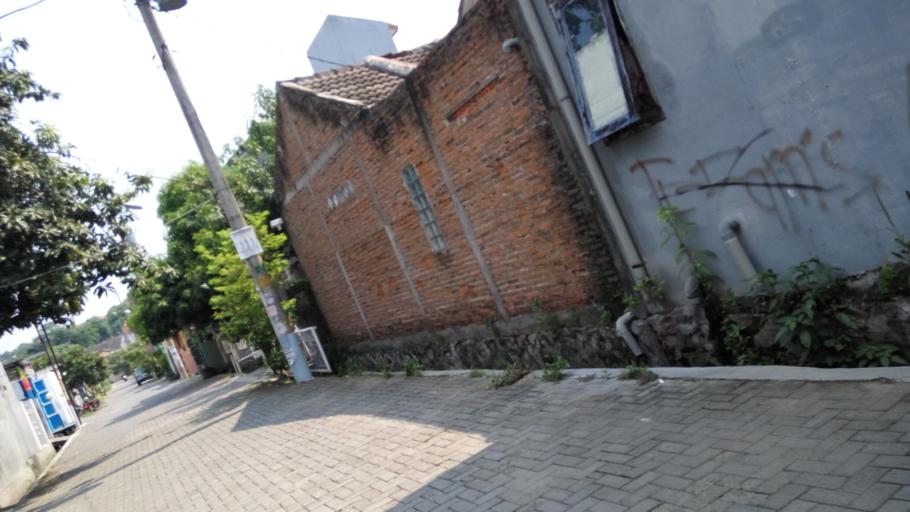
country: ID
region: Central Java
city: Mranggen
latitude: -7.0380
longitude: 110.4762
